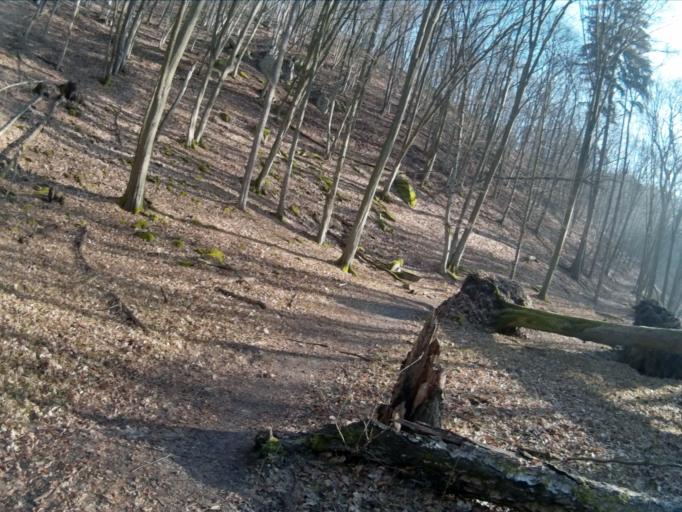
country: CZ
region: Vysocina
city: Namest' nad Oslavou
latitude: 49.1686
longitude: 16.1702
